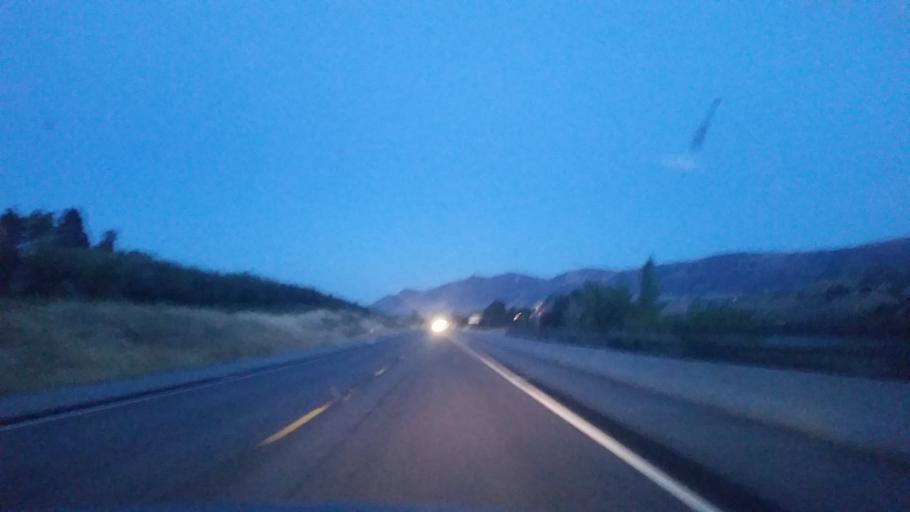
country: US
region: Washington
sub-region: Chelan County
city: South Wenatchee
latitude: 47.3907
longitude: -120.2720
